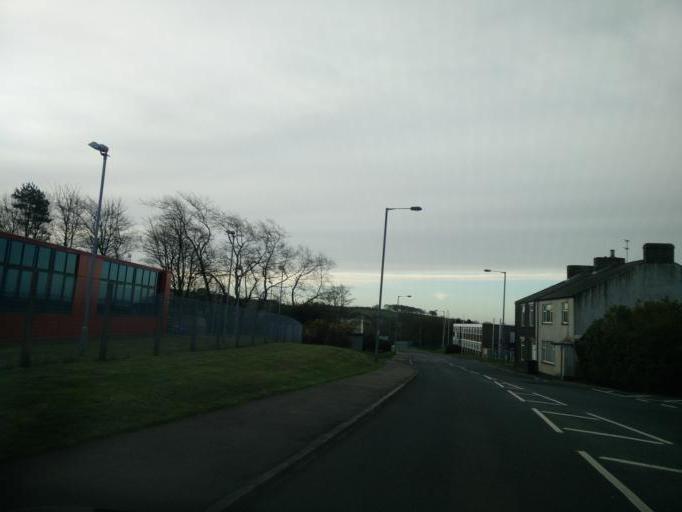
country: GB
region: England
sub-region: County Durham
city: Crook
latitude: 54.7070
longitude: -1.7513
